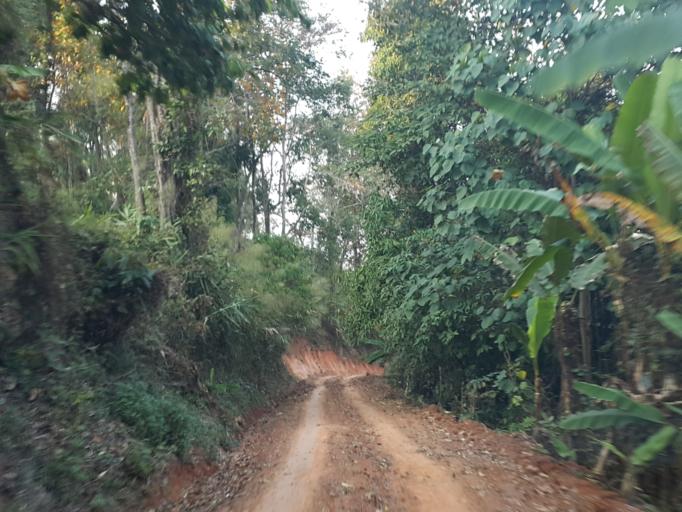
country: TH
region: Chiang Mai
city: Mae Taeng
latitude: 19.0424
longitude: 98.7675
